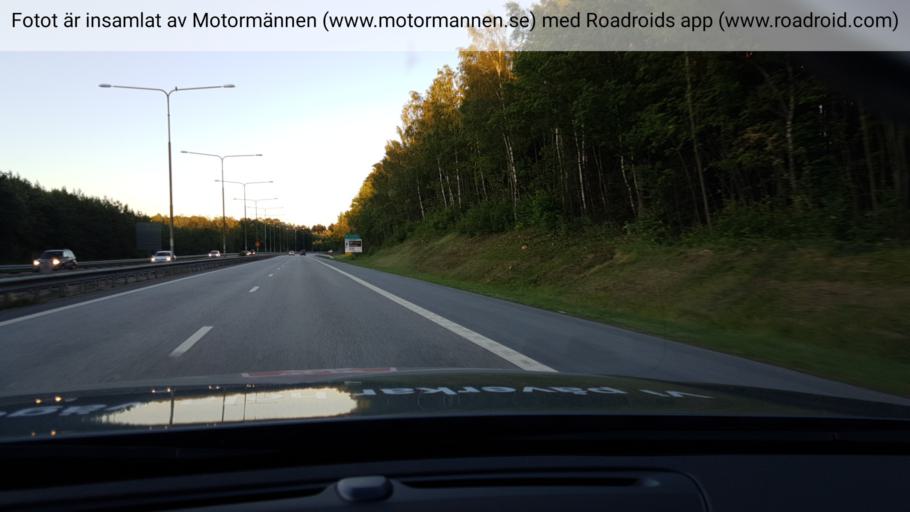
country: SE
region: Vaestmanland
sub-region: Vasteras
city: Vasteras
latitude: 59.6142
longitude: 16.4942
